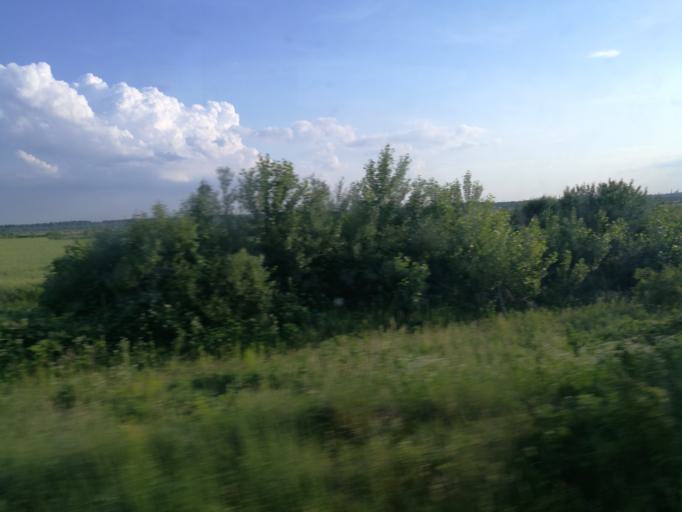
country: RO
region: Arges
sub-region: Comuna Calinesti
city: Gorganu
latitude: 44.8224
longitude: 25.0235
